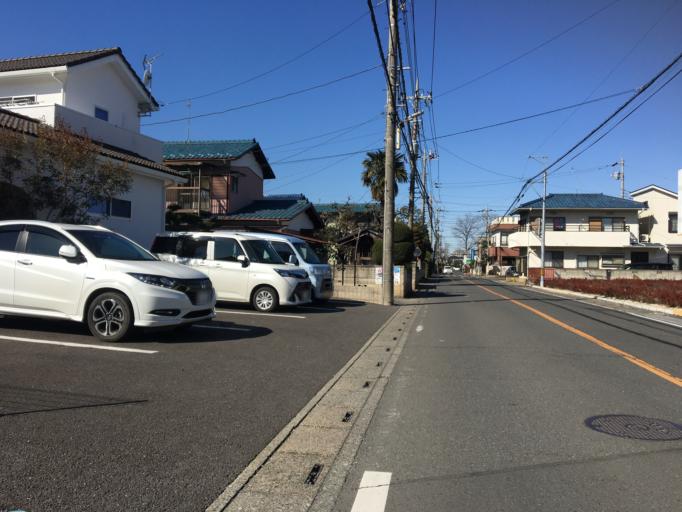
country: JP
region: Saitama
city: Oi
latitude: 35.8576
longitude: 139.5130
